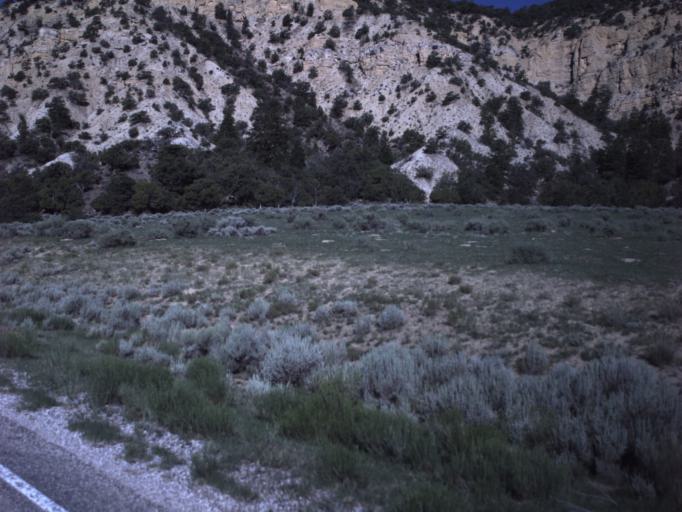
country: US
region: Utah
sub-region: Wayne County
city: Loa
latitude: 38.6695
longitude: -111.4231
